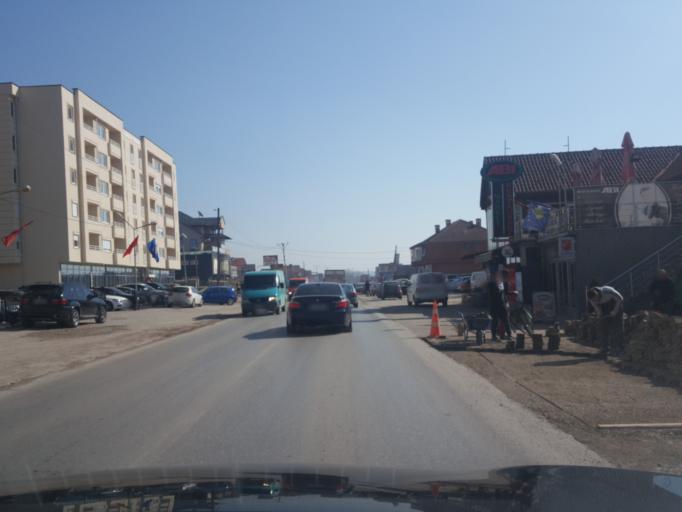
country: XK
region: Mitrovica
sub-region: Vushtrri
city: Vushtrri
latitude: 42.8263
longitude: 20.9711
